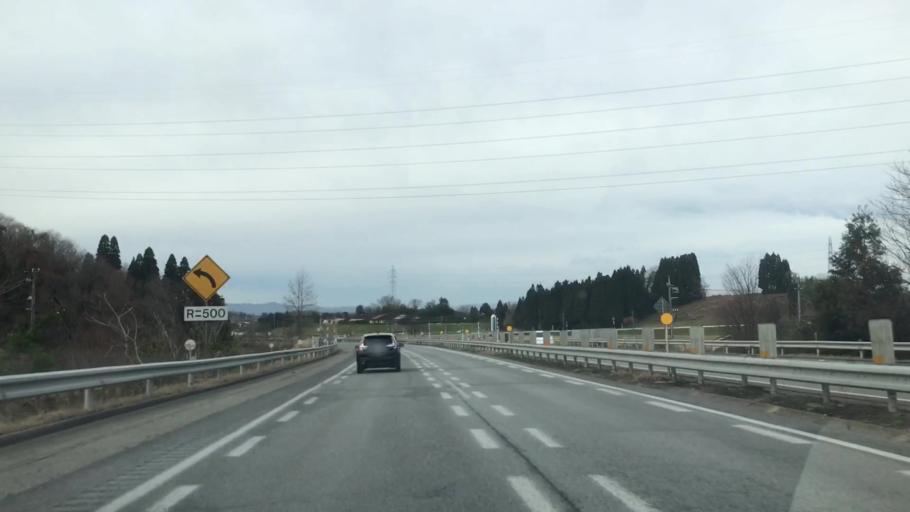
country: JP
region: Toyama
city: Kuragaki-kosugi
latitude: 36.6895
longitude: 137.0969
